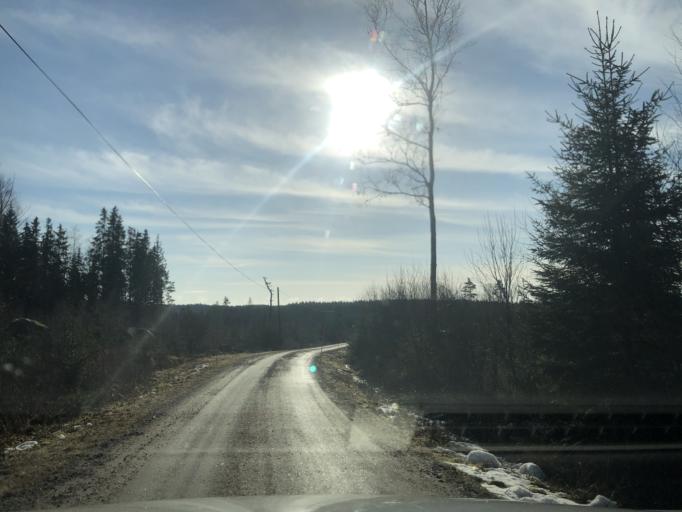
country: SE
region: Vaestra Goetaland
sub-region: Ulricehamns Kommun
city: Ulricehamn
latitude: 57.7936
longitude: 13.4662
